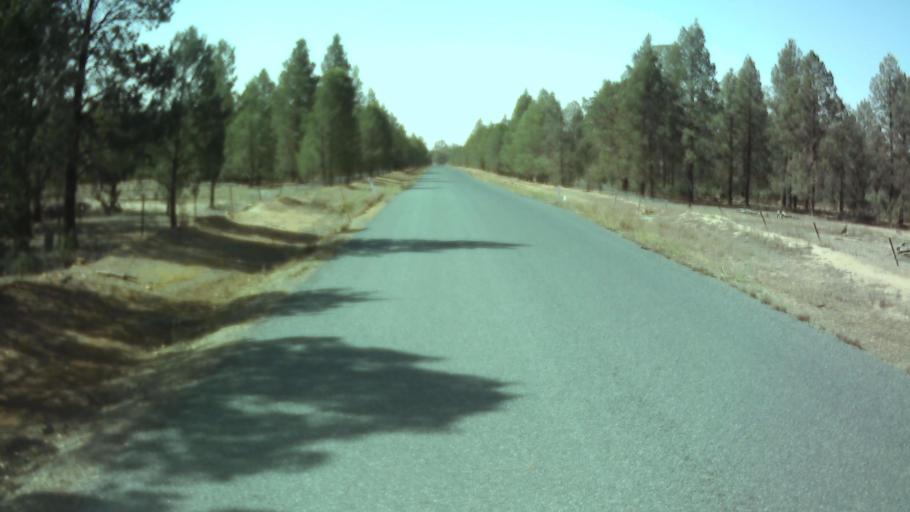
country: AU
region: New South Wales
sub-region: Weddin
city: Grenfell
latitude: -33.9058
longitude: 147.9198
